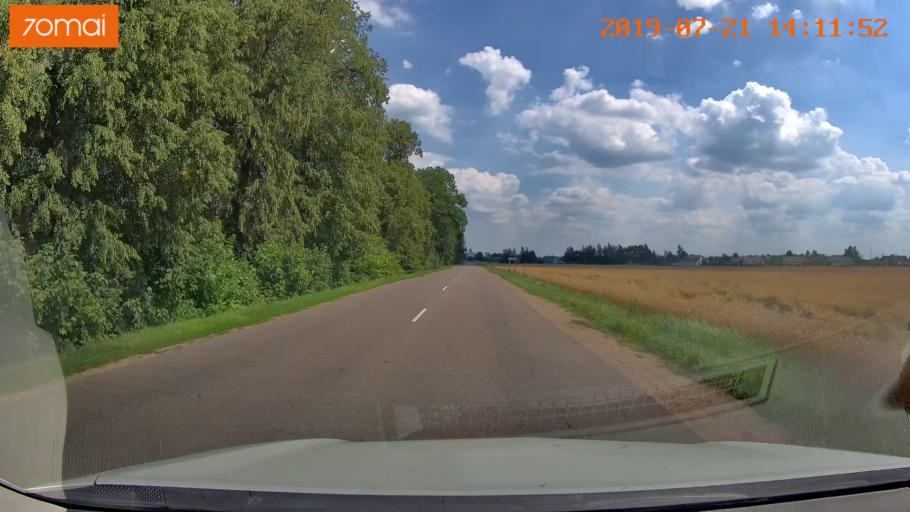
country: BY
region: Grodnenskaya
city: Karelichy
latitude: 53.6549
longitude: 26.1605
